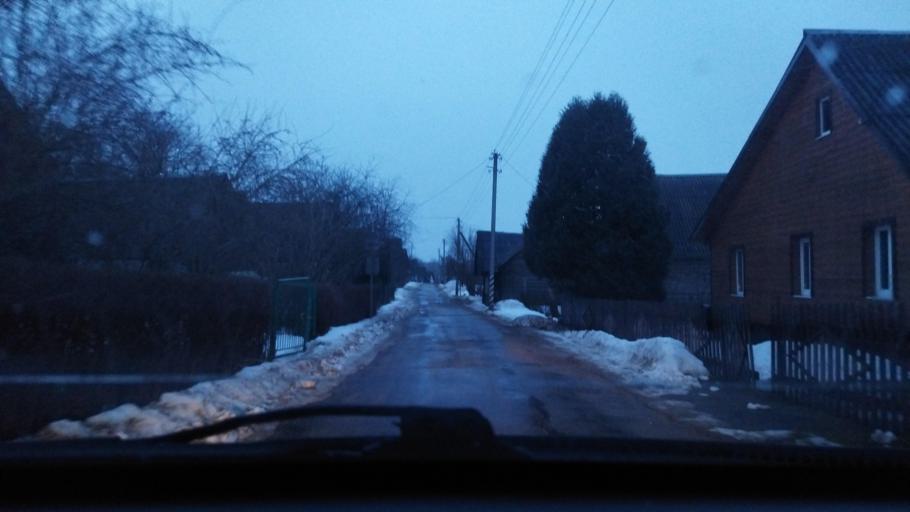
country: BY
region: Minsk
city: Svir
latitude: 54.9410
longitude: 26.4028
